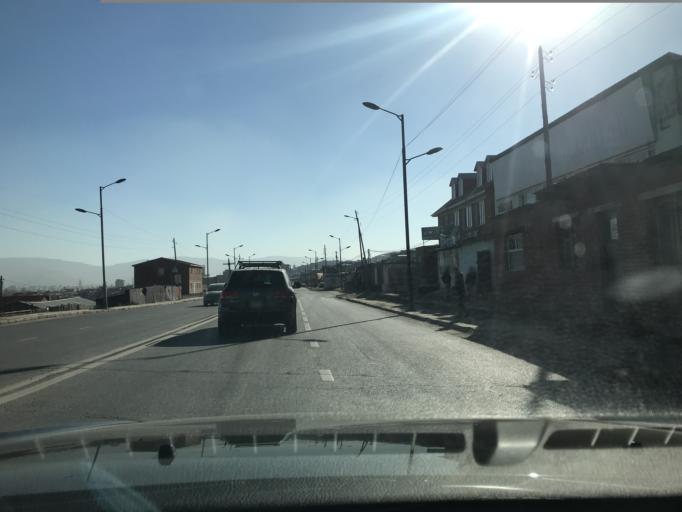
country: MN
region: Ulaanbaatar
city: Ulaanbaatar
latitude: 47.9750
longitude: 106.9182
